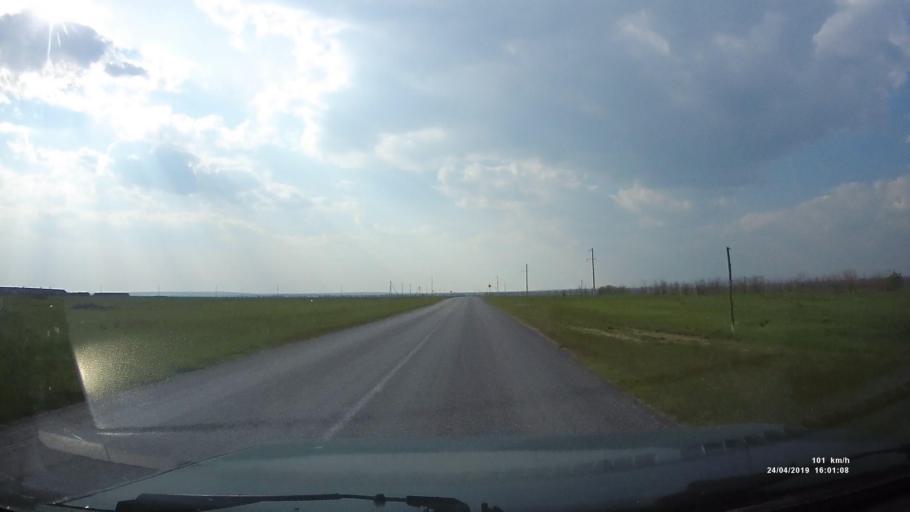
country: RU
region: Rostov
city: Sovetskoye
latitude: 46.6391
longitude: 42.4411
